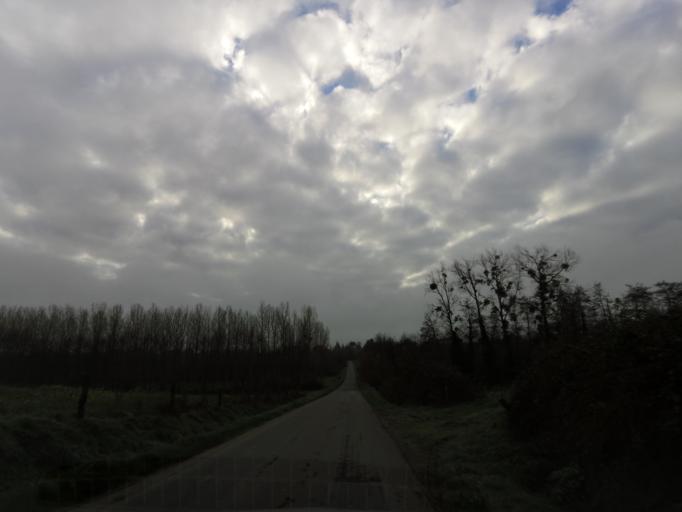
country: FR
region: Brittany
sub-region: Departement d'Ille-et-Vilaine
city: Chanteloup
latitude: 47.9666
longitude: -1.6389
